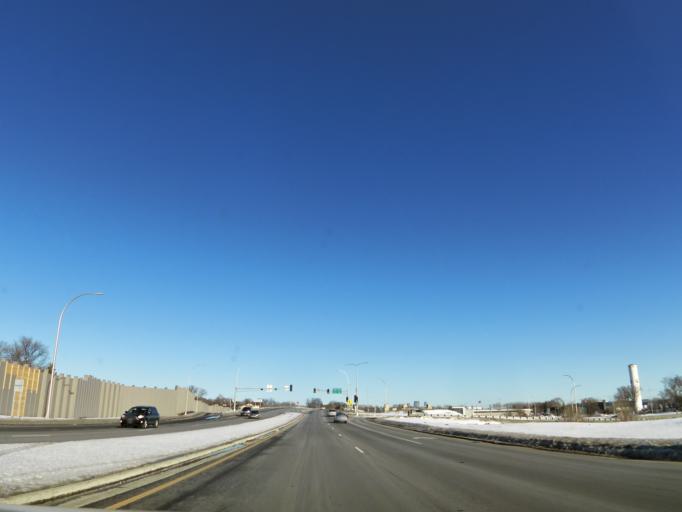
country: US
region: Minnesota
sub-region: Hennepin County
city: Saint Louis Park
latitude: 44.9417
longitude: -93.3511
